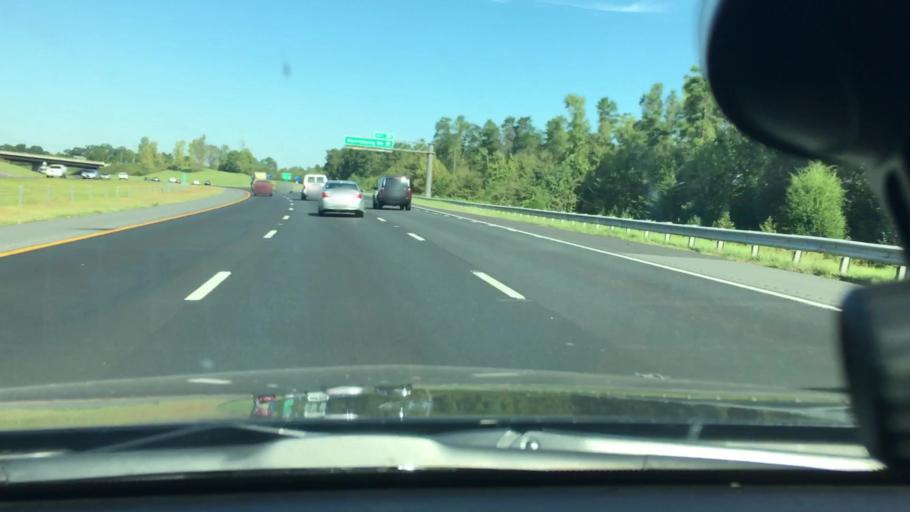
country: US
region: North Carolina
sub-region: Mecklenburg County
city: Mint Hill
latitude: 35.2489
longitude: -80.6505
